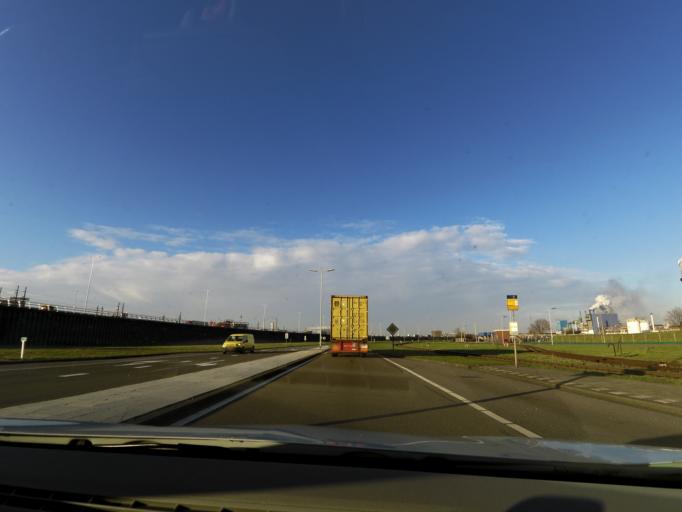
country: NL
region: South Holland
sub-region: Gemeente Maassluis
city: Maassluis
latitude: 51.8838
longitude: 4.2604
